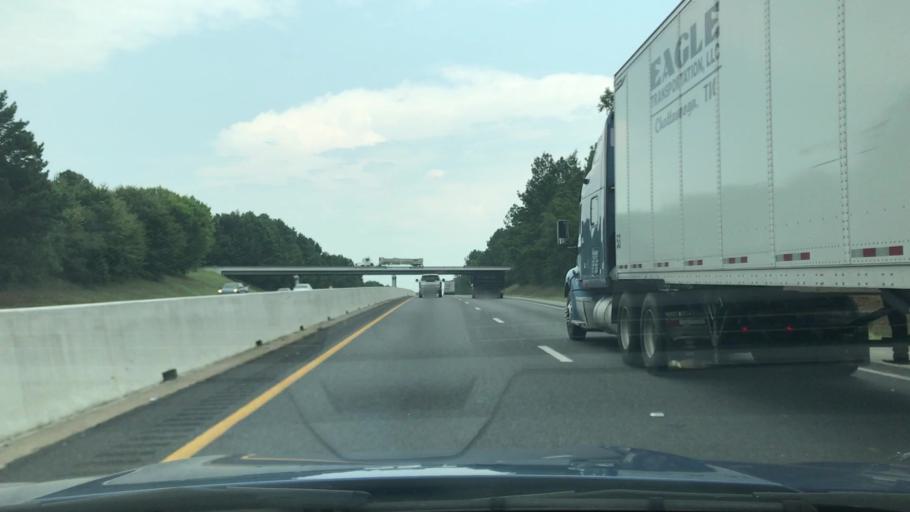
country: US
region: Texas
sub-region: Gregg County
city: Liberty City
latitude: 32.4358
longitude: -94.9734
